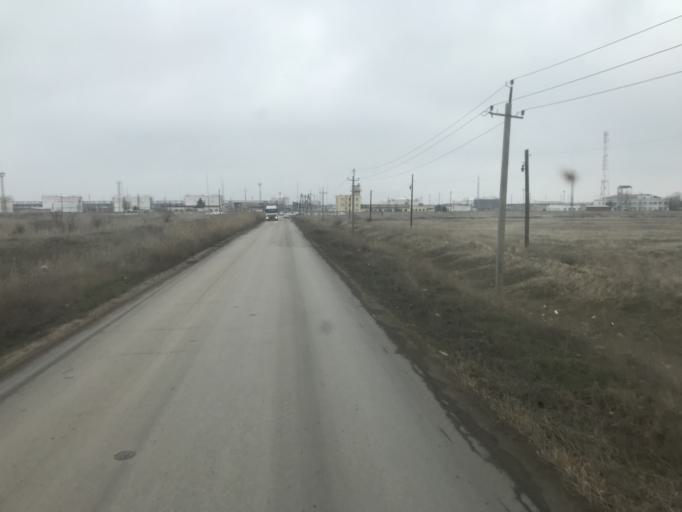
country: RU
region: Volgograd
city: Svetlyy Yar
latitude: 48.5022
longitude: 44.6446
